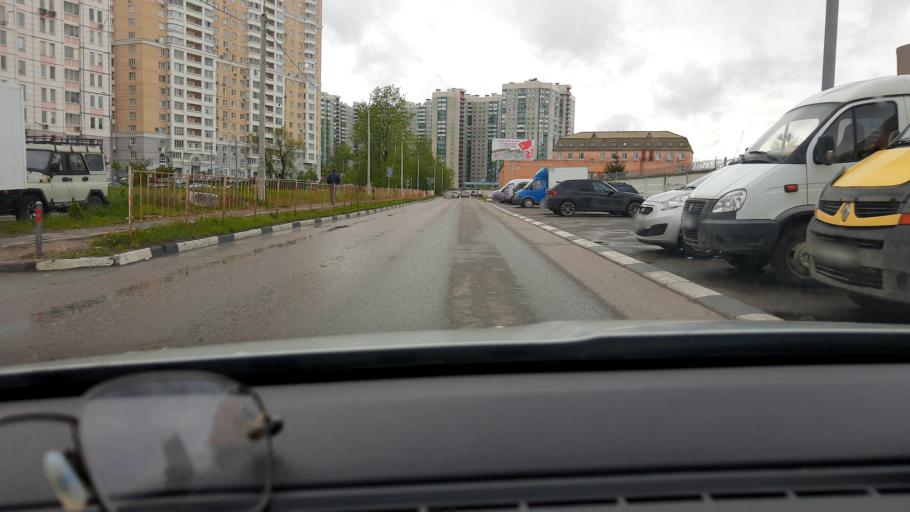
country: RU
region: Moskovskaya
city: Opalikha
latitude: 55.8335
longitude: 37.2886
